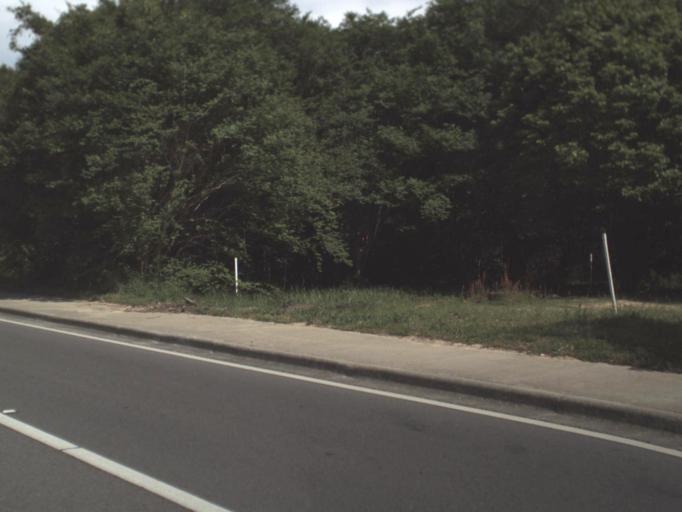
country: US
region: Florida
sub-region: Santa Rosa County
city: East Milton
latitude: 30.6342
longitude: -86.9754
